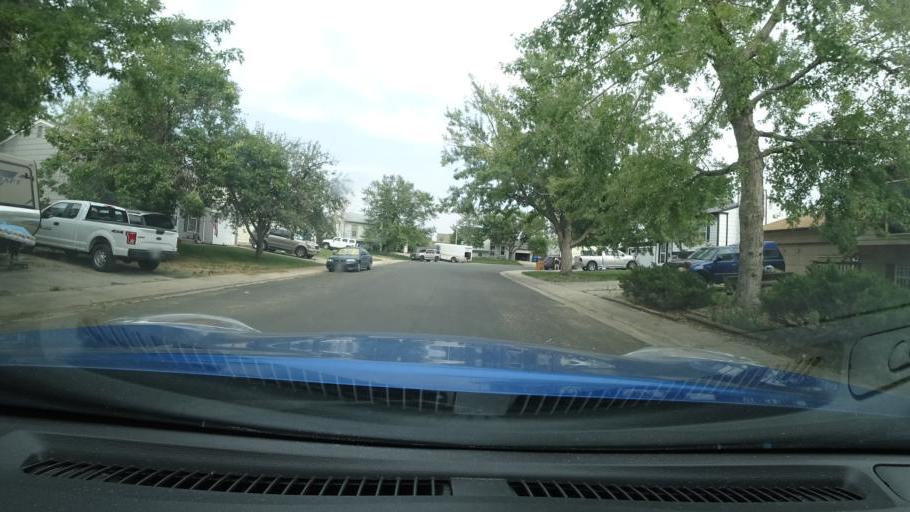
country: US
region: Colorado
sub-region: Adams County
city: Aurora
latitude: 39.7486
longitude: -104.7640
